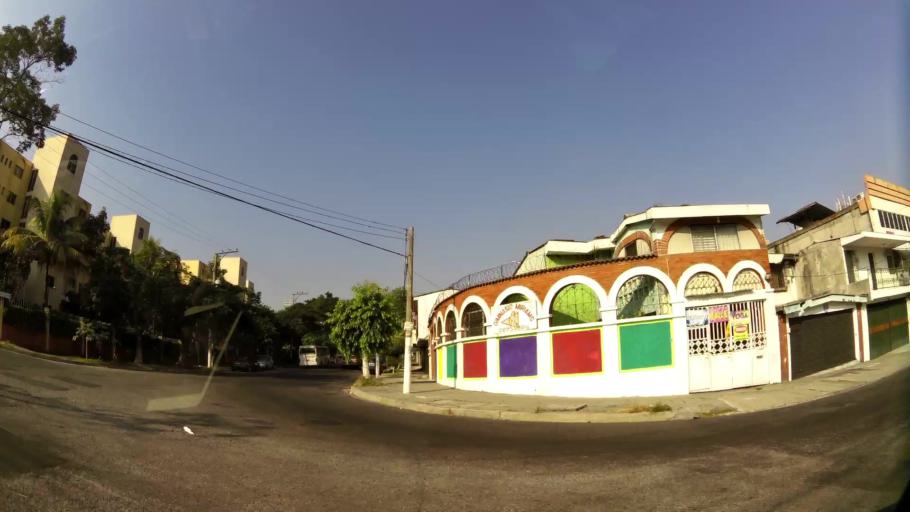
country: SV
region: San Salvador
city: San Salvador
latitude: 13.6828
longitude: -89.2190
